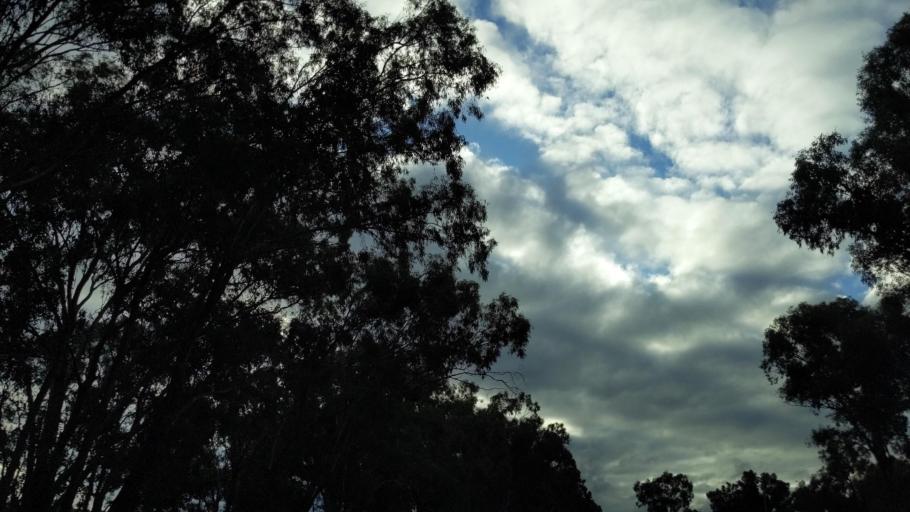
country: AU
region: New South Wales
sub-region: Wagga Wagga
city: Wagga Wagga
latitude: -35.0591
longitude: 147.3747
